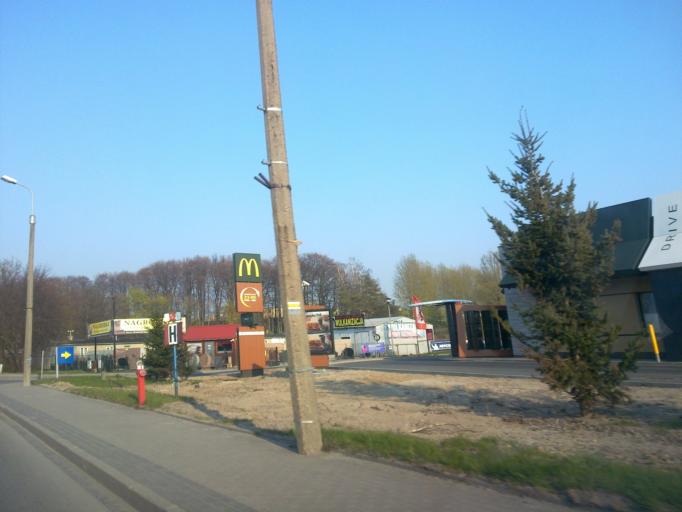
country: PL
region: Pomeranian Voivodeship
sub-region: Powiat pucki
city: Puck
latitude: 54.7183
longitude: 18.3930
